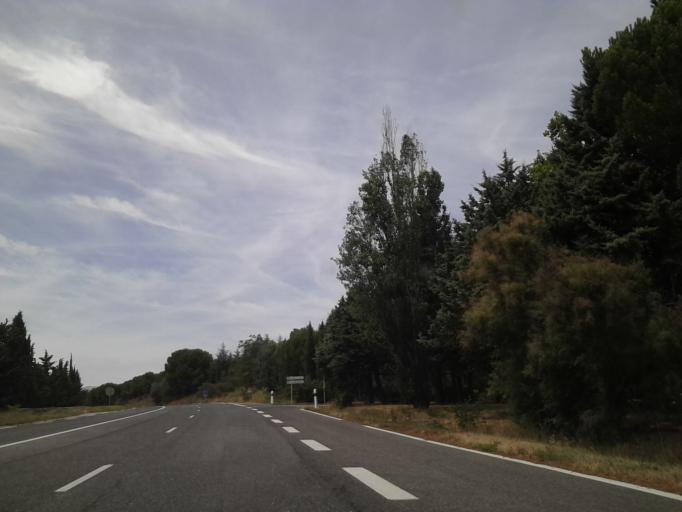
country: FR
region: Languedoc-Roussillon
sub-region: Departement des Pyrenees-Orientales
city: Vinca
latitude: 42.6525
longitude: 2.5470
